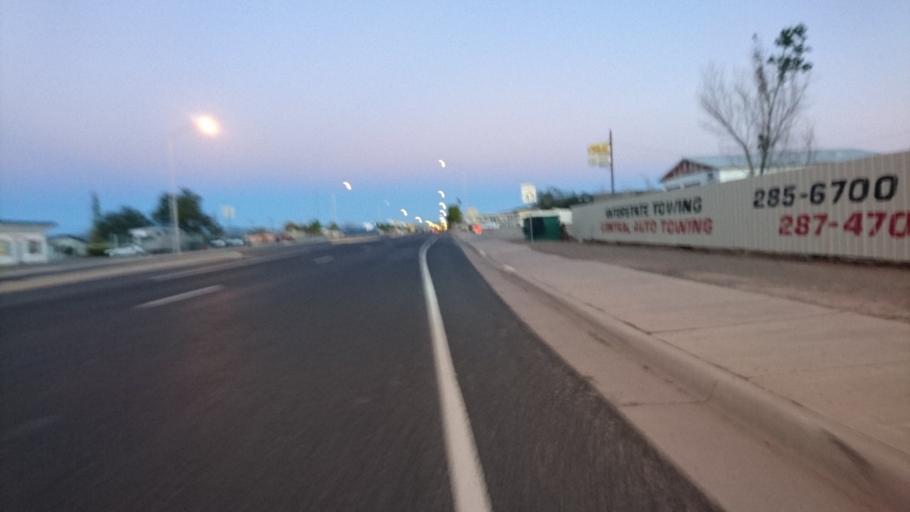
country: US
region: New Mexico
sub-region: Cibola County
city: Grants
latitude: 35.1407
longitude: -107.8303
